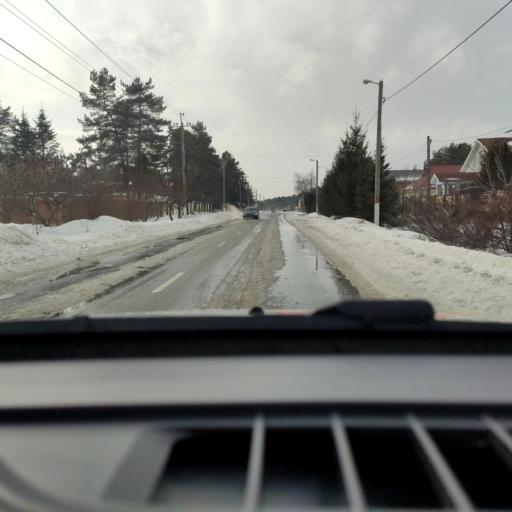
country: RU
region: Voronezj
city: Podgornoye
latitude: 51.7804
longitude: 39.1347
